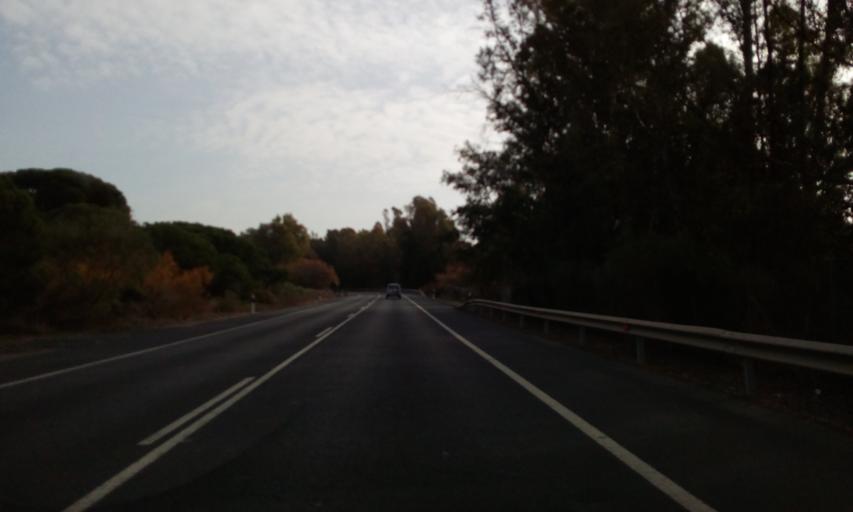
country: ES
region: Andalusia
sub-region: Provincia de Huelva
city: Palos de la Frontera
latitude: 37.1653
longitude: -6.8899
